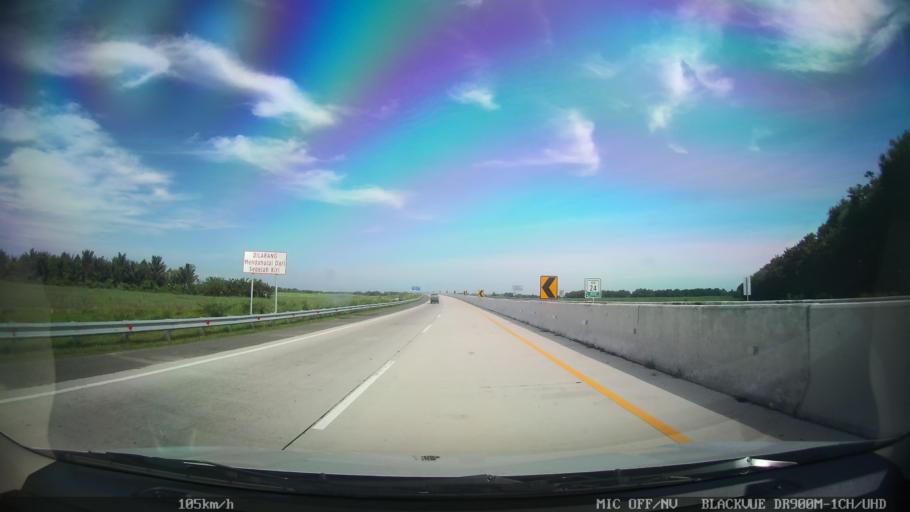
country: ID
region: North Sumatra
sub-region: Kabupaten Langkat
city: Stabat
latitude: 3.7045
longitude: 98.5381
